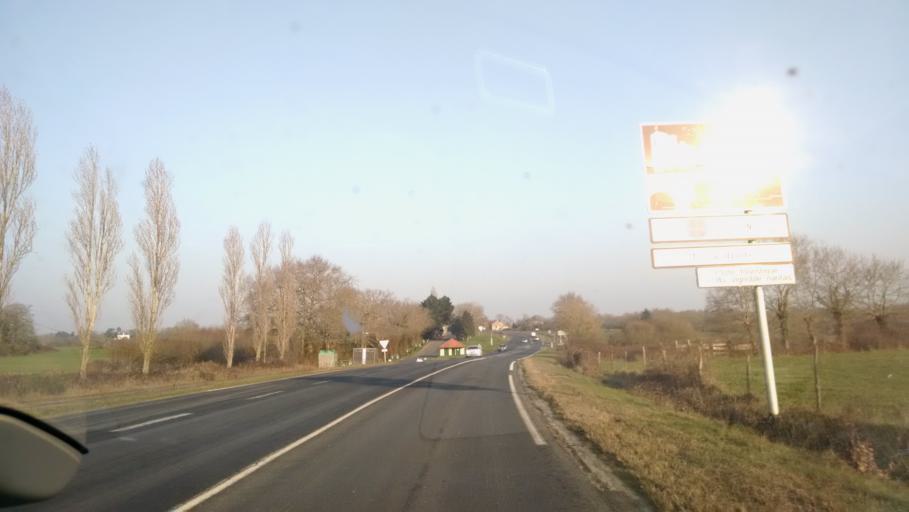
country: FR
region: Pays de la Loire
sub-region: Departement de la Loire-Atlantique
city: Aigrefeuille-sur-Maine
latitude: 47.0679
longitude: -1.3910
